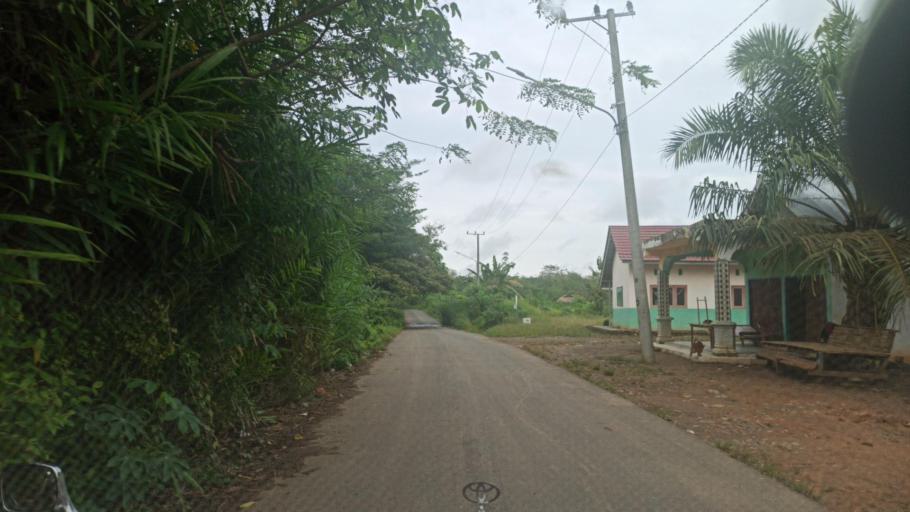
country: ID
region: South Sumatra
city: Gunungmegang Dalam
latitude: -3.3072
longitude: 103.6683
